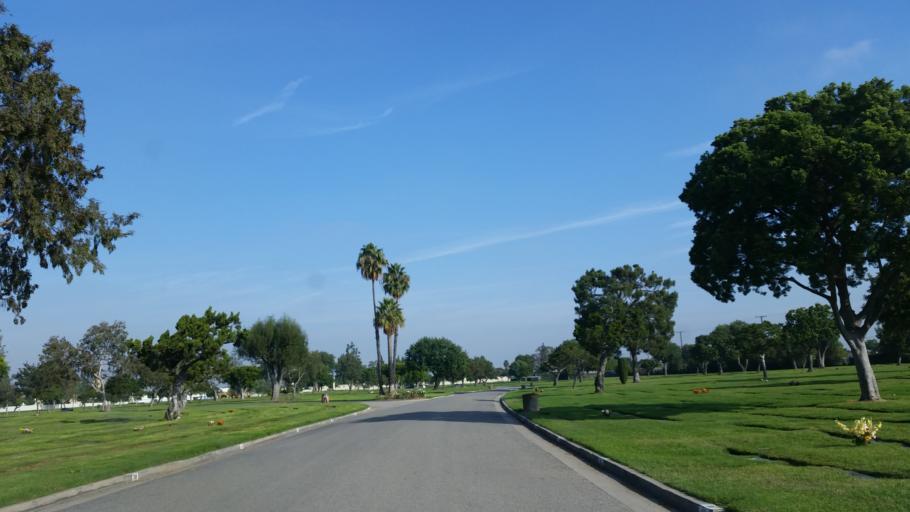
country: US
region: California
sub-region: Los Angeles County
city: Lakewood
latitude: 33.8394
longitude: -118.1655
